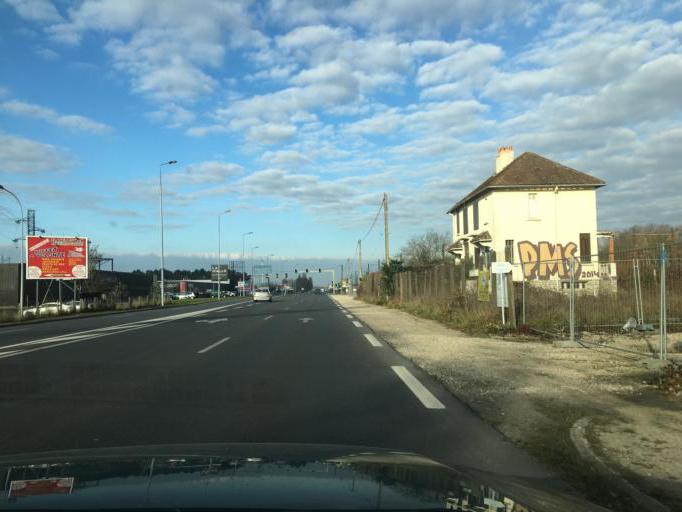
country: FR
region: Centre
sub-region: Departement du Loiret
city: Saran
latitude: 47.9629
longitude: 1.8889
